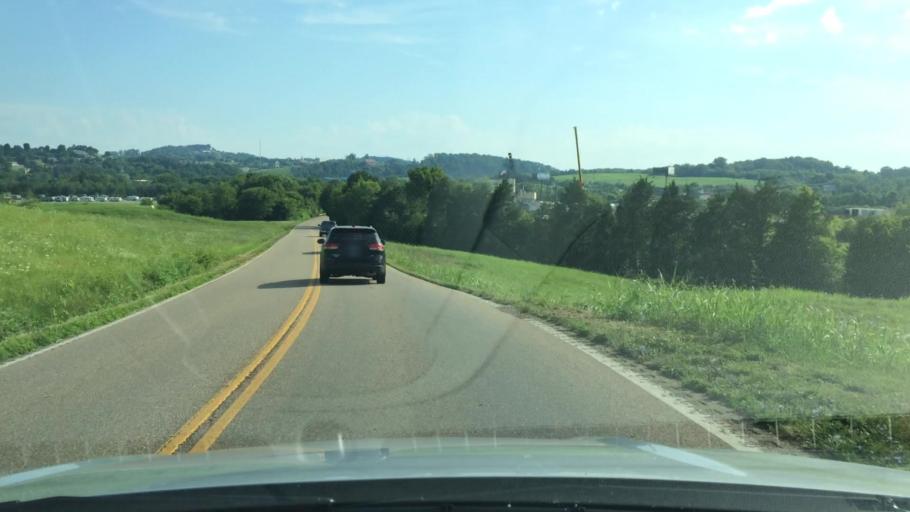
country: US
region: Tennessee
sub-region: Sevier County
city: Sevierville
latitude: 35.9240
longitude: -83.5900
